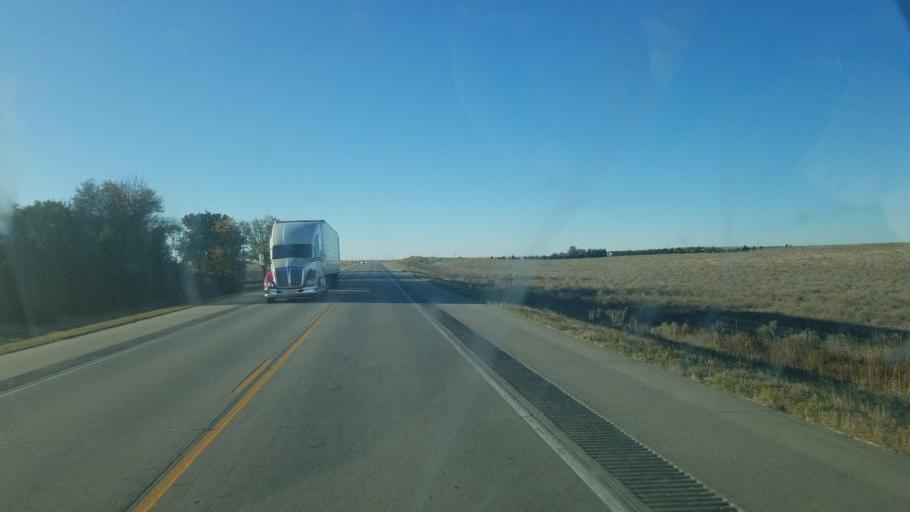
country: US
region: Colorado
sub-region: Kiowa County
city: Eads
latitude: 38.5909
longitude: -102.7861
